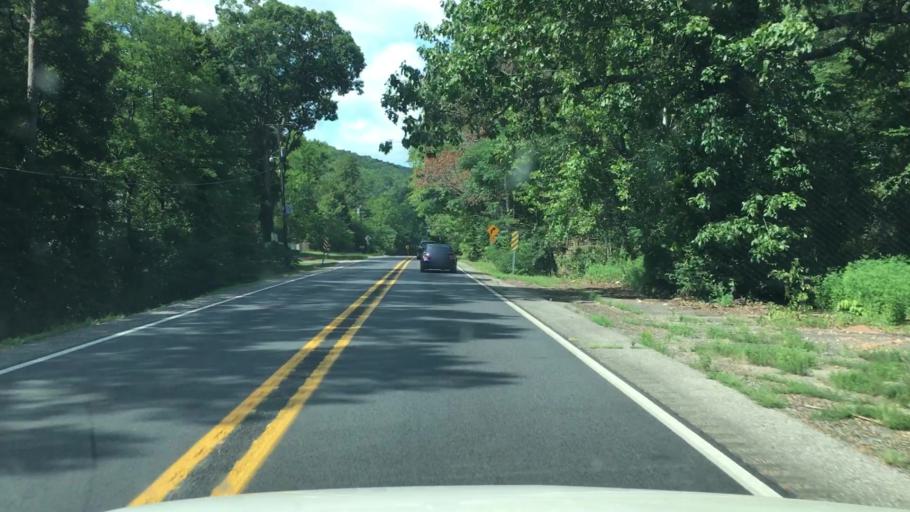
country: US
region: Arkansas
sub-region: Garland County
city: Lake Hamilton
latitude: 34.3884
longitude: -93.1211
